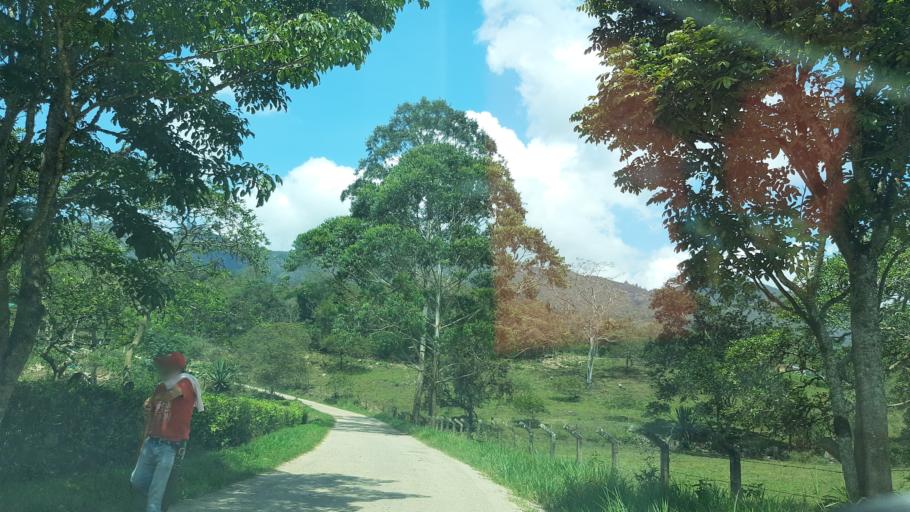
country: CO
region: Boyaca
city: Chinavita
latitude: 5.1327
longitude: -73.3649
